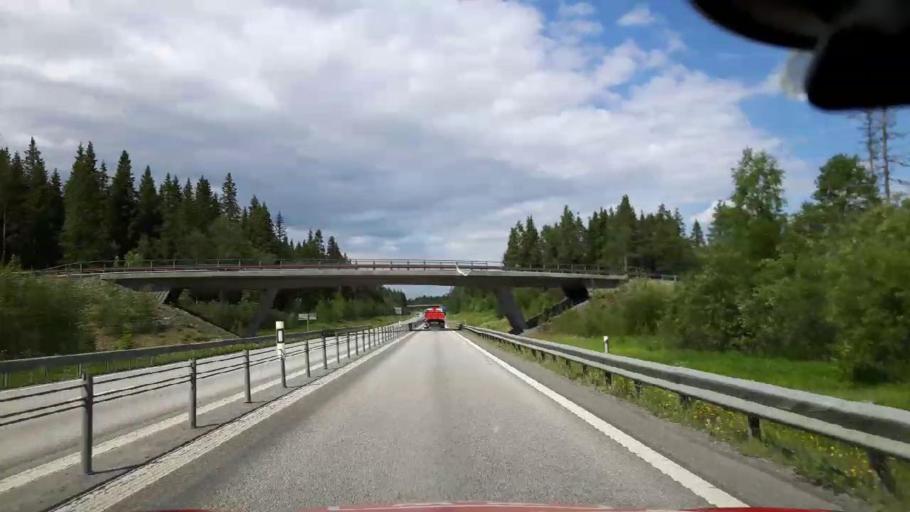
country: SE
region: Jaemtland
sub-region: OEstersunds Kommun
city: Ostersund
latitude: 63.2069
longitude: 14.6702
